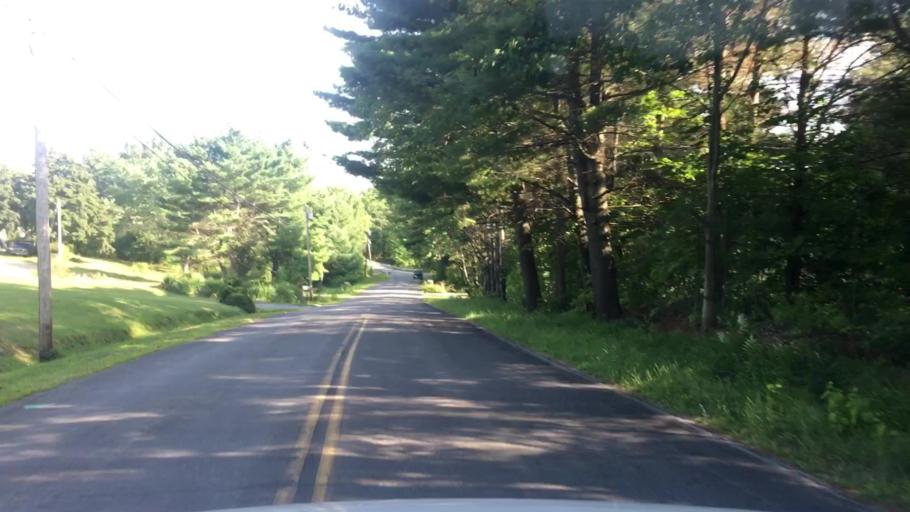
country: US
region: Maine
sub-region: Kennebec County
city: Waterville
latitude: 44.5822
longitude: -69.6724
